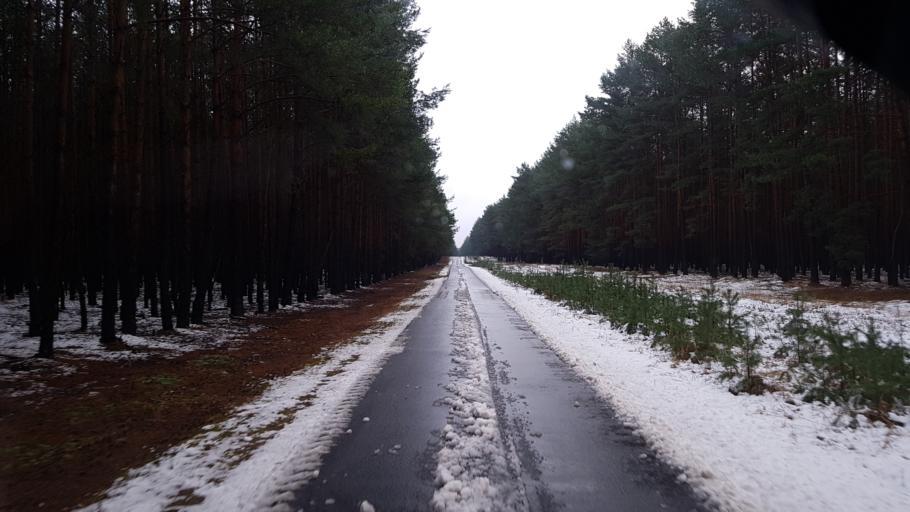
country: DE
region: Brandenburg
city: Straupitz
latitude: 51.9630
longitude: 14.1514
